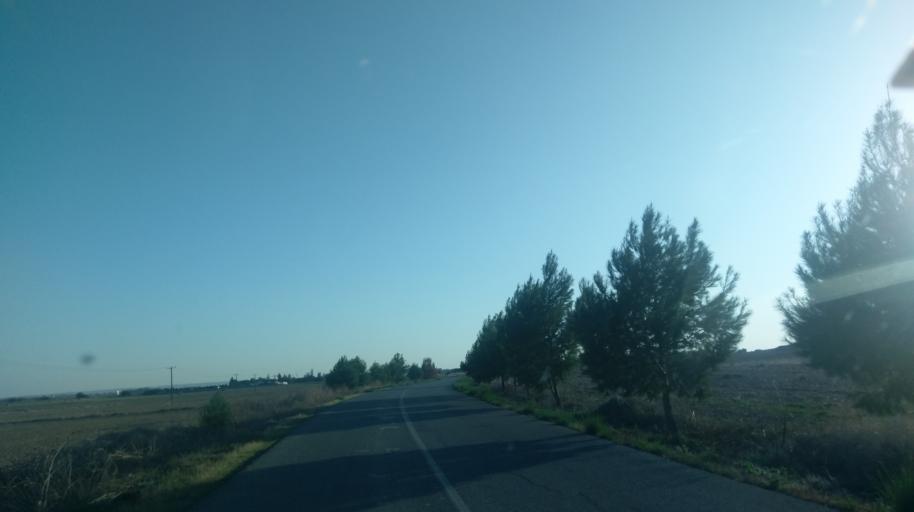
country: CY
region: Ammochostos
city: Lefkonoiko
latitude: 35.2002
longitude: 33.6194
